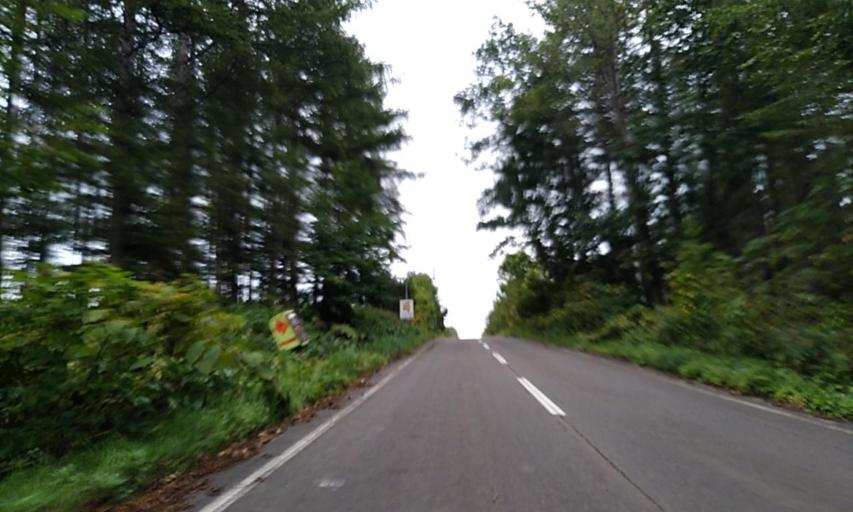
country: JP
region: Hokkaido
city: Obihiro
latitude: 42.6680
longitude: 143.0608
